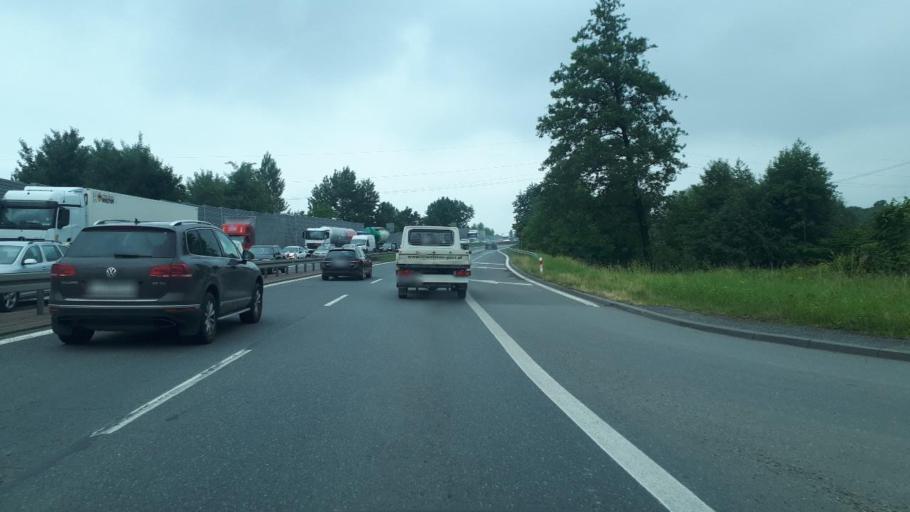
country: PL
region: Silesian Voivodeship
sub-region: Powiat bielski
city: Czechowice-Dziedzice
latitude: 49.9186
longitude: 18.9892
